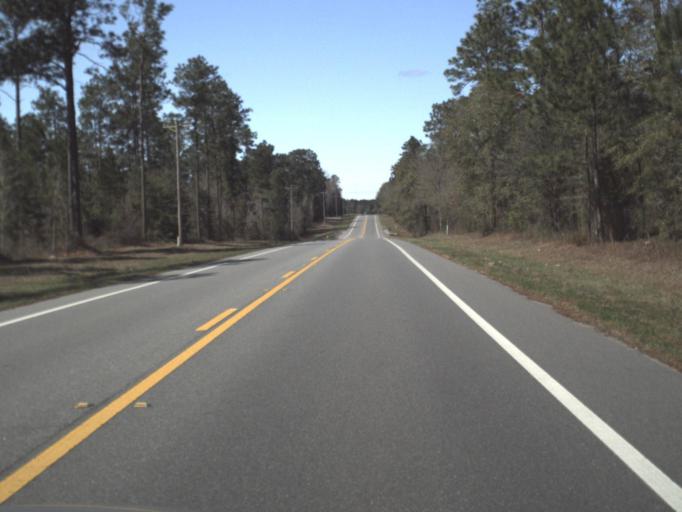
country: US
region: Florida
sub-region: Gadsden County
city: Gretna
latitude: 30.6688
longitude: -84.6997
